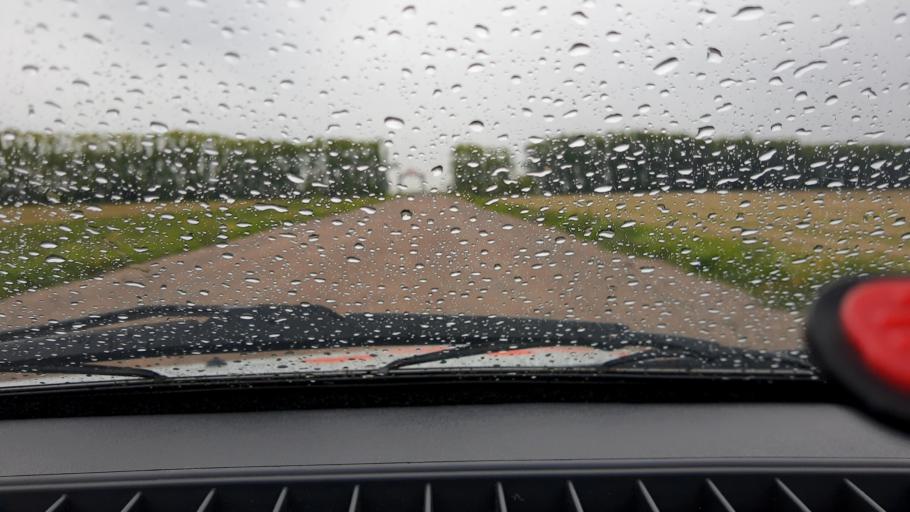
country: RU
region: Bashkortostan
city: Karmaskaly
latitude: 54.3856
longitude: 56.1203
